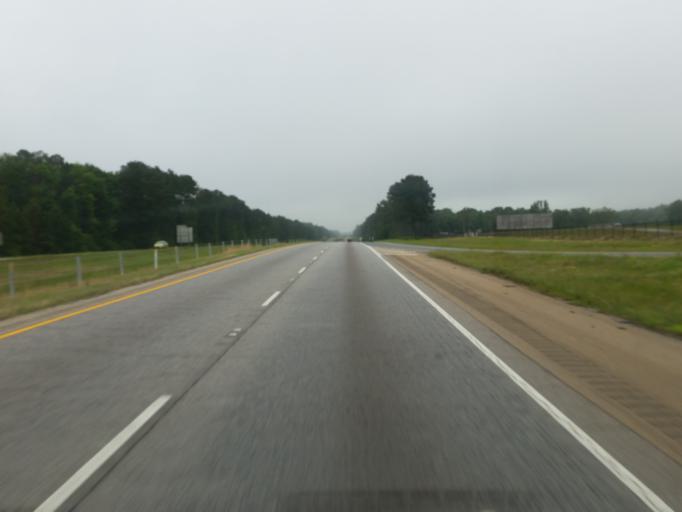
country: US
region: Louisiana
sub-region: Webster Parish
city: Minden
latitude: 32.5799
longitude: -93.2456
